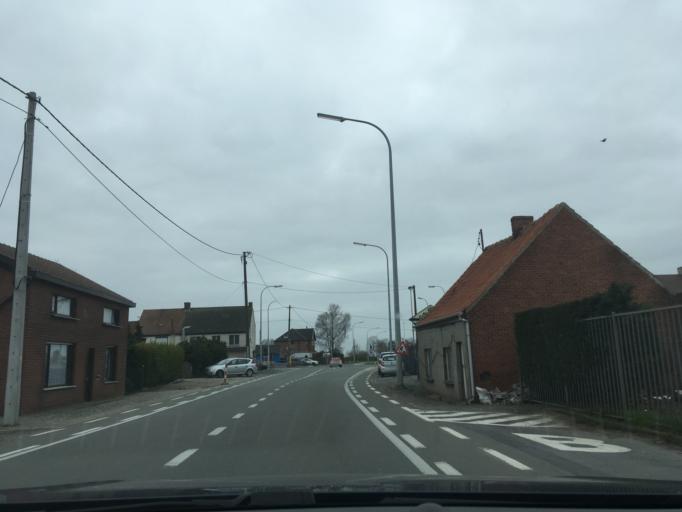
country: BE
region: Flanders
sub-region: Provincie West-Vlaanderen
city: Lichtervelde
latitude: 51.0237
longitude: 3.1131
